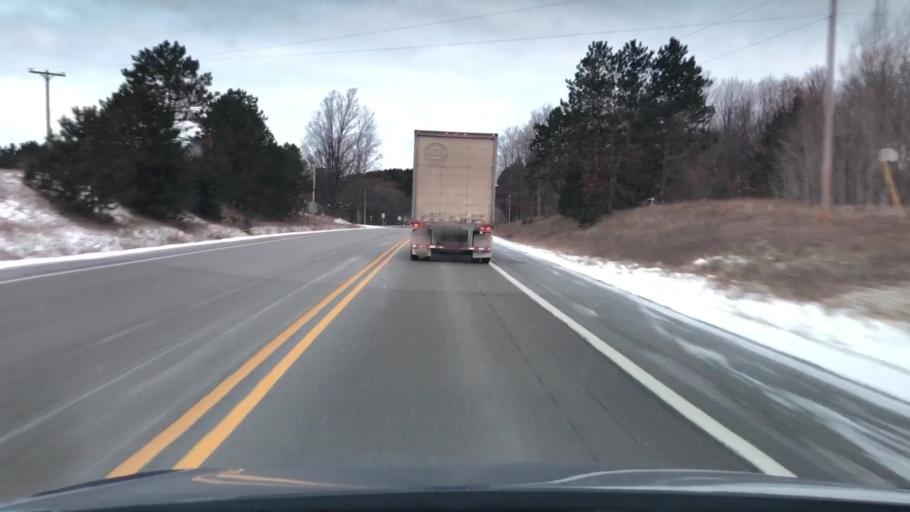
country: US
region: Michigan
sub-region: Wexford County
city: Cadillac
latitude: 44.1784
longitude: -85.3785
